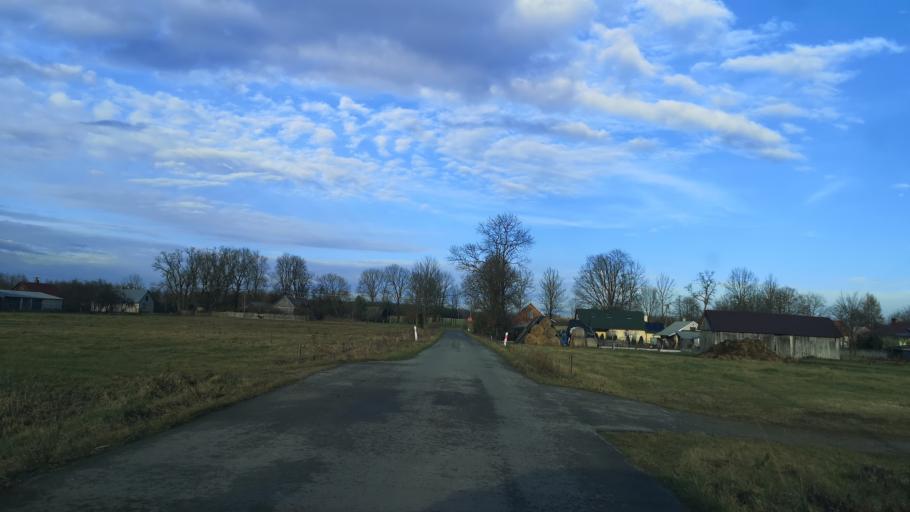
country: PL
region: Subcarpathian Voivodeship
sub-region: Powiat lezajski
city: Piskorowice
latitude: 50.2623
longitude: 22.5878
